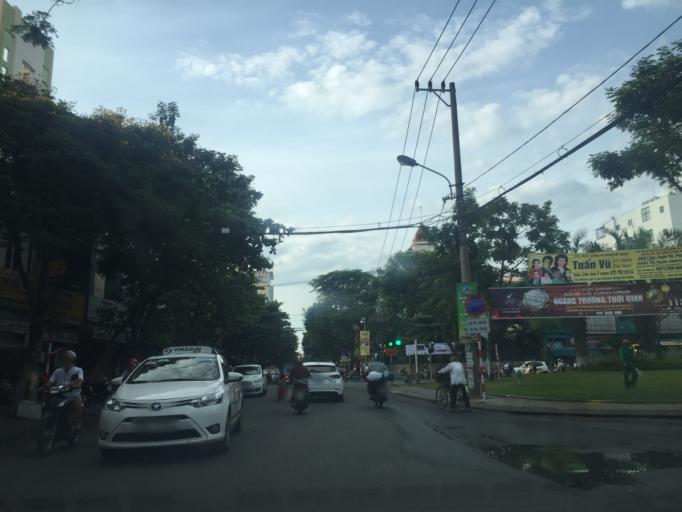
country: VN
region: Da Nang
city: Da Nang
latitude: 16.0722
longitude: 108.2131
